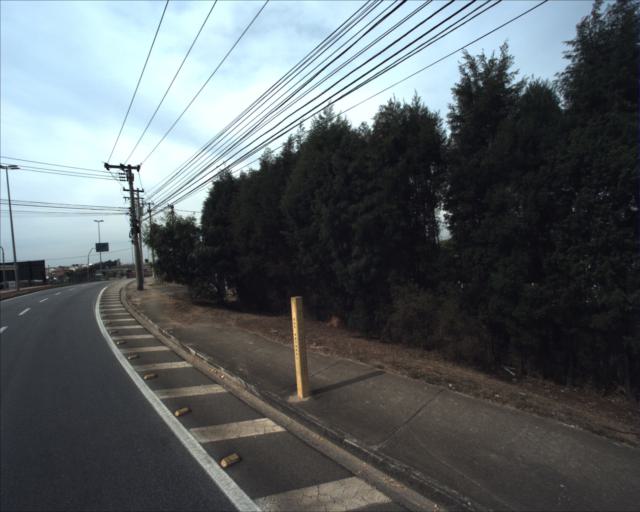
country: BR
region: Sao Paulo
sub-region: Sorocaba
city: Sorocaba
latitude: -23.4555
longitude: -47.4510
